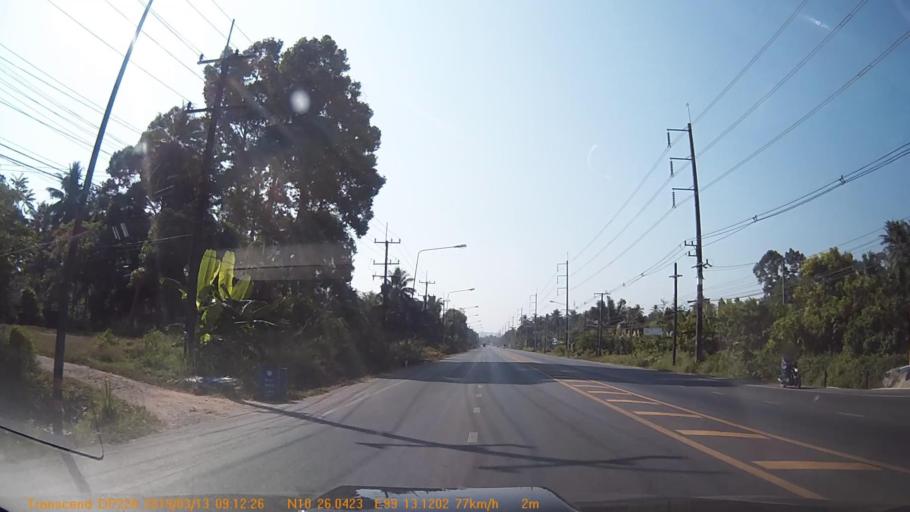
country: TH
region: Chumphon
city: Chumphon
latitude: 10.4338
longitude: 99.2188
